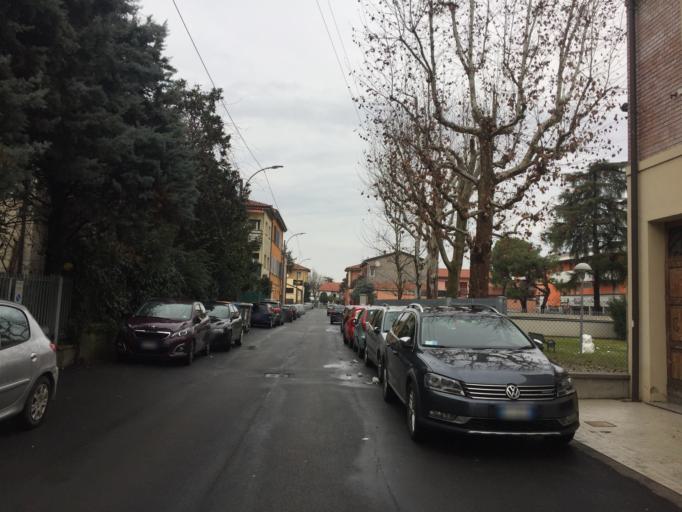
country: IT
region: Emilia-Romagna
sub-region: Provincia di Bologna
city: Casalecchio di Reno
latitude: 44.5088
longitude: 11.2988
